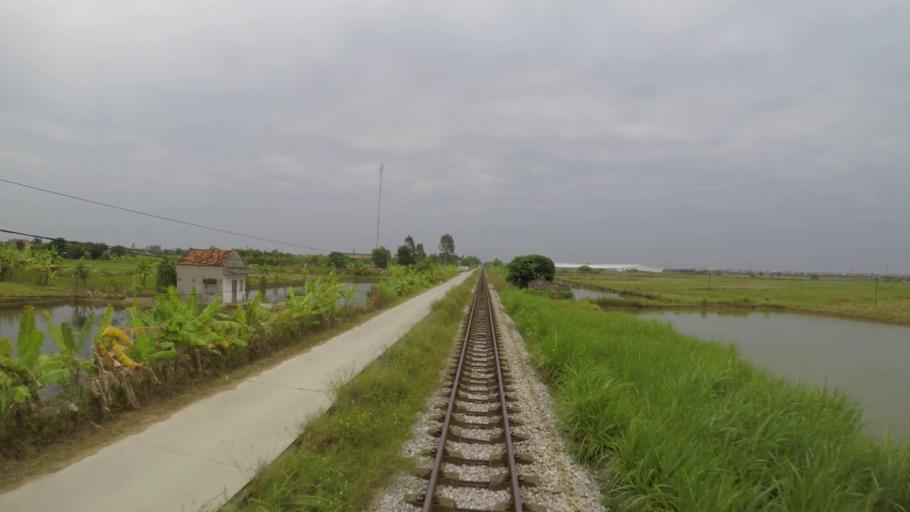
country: VN
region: Hai Duong
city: Lai Cach
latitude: 20.9530
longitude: 106.2280
